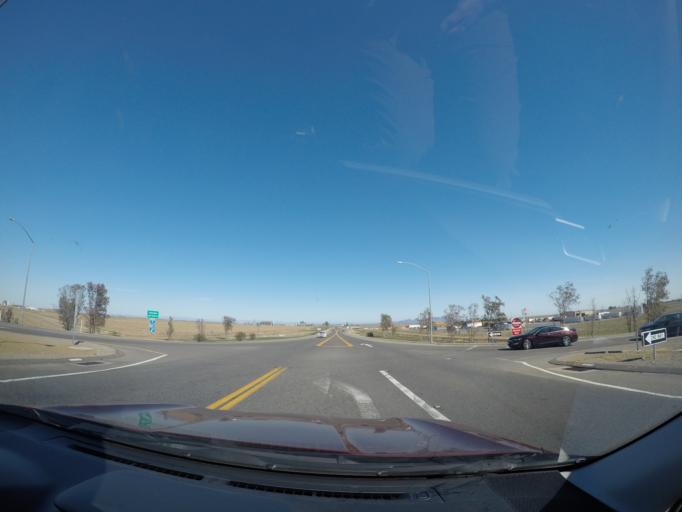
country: US
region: California
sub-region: Colusa County
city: Williams
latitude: 39.1674
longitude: -122.1481
